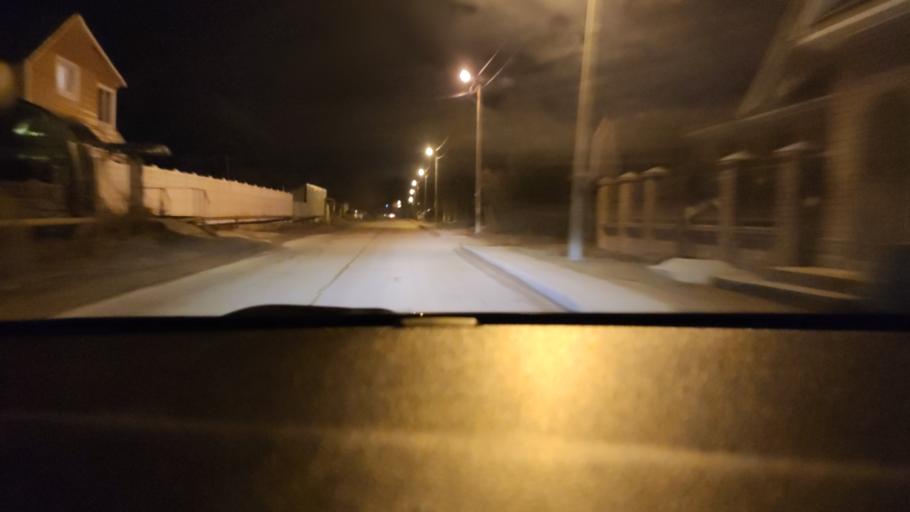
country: RU
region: Tatarstan
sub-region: Gorod Kazan'
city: Kazan
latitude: 55.8460
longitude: 49.1975
